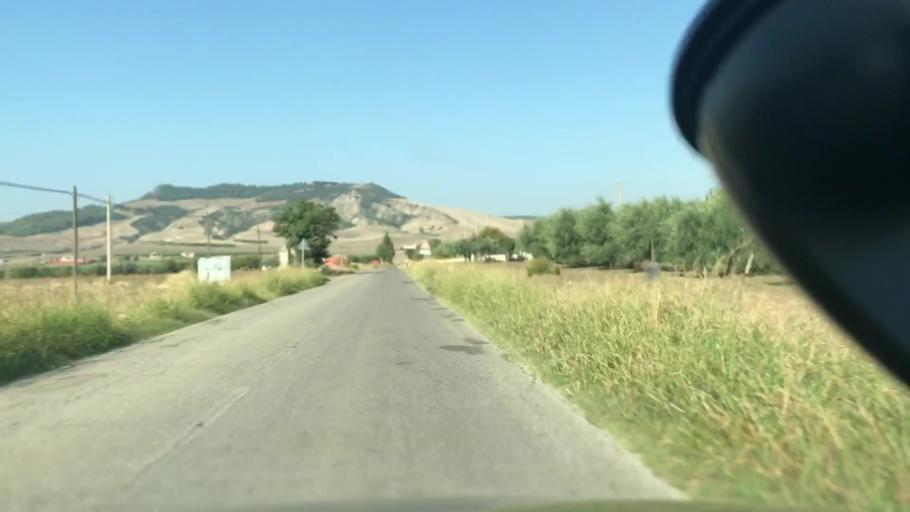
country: IT
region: Basilicate
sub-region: Provincia di Matera
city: La Martella
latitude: 40.6583
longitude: 16.5287
